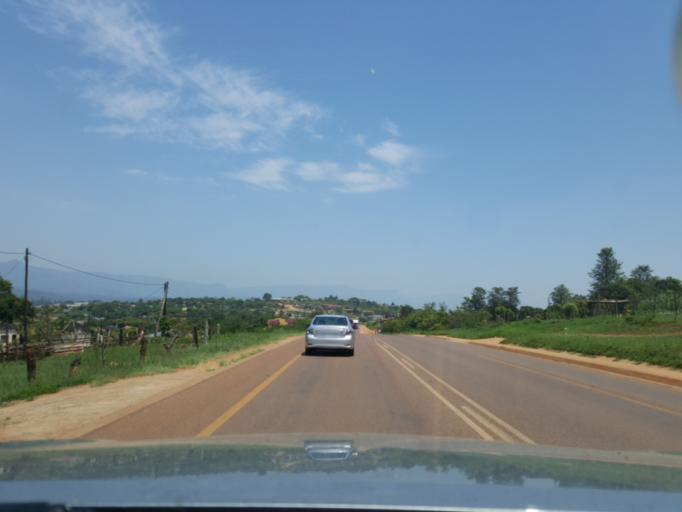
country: ZA
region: Limpopo
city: Thulamahashi
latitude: -24.8503
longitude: 31.1041
